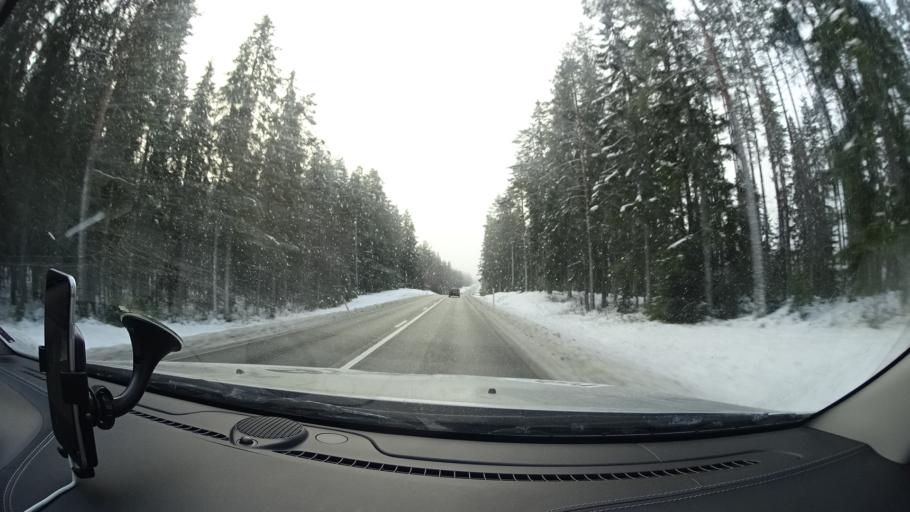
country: SE
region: OErebro
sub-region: Ljusnarsbergs Kommun
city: Kopparberg
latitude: 59.9056
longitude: 15.0210
